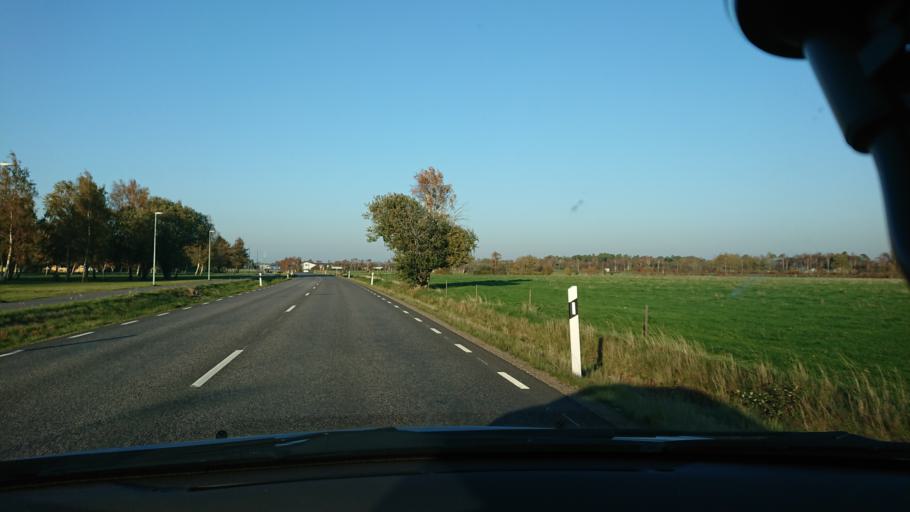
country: SE
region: Halland
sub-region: Laholms Kommun
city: Mellbystrand
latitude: 56.4491
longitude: 12.9329
